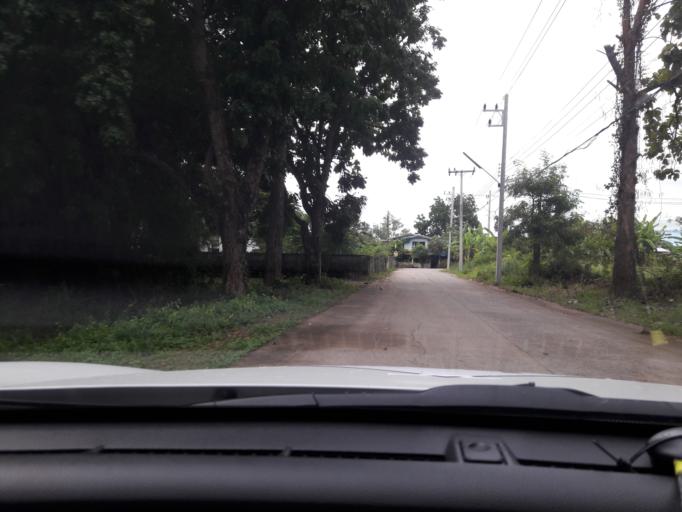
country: TH
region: Nakhon Sawan
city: Tak Fa
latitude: 15.3523
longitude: 100.4944
